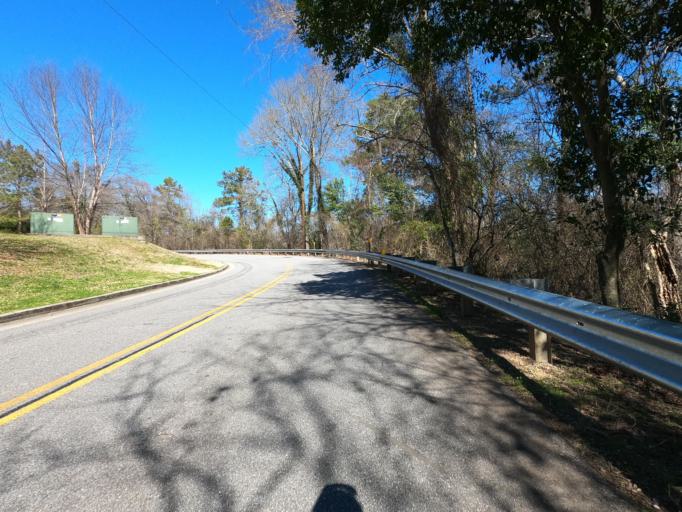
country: US
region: Georgia
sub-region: Clarke County
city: Athens
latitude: 33.9460
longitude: -83.3693
